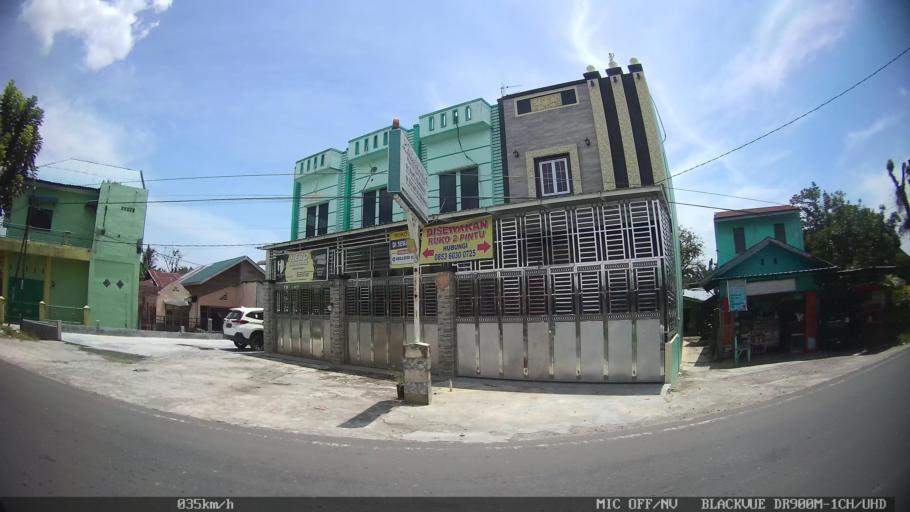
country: ID
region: North Sumatra
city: Binjai
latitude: 3.5998
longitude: 98.4978
